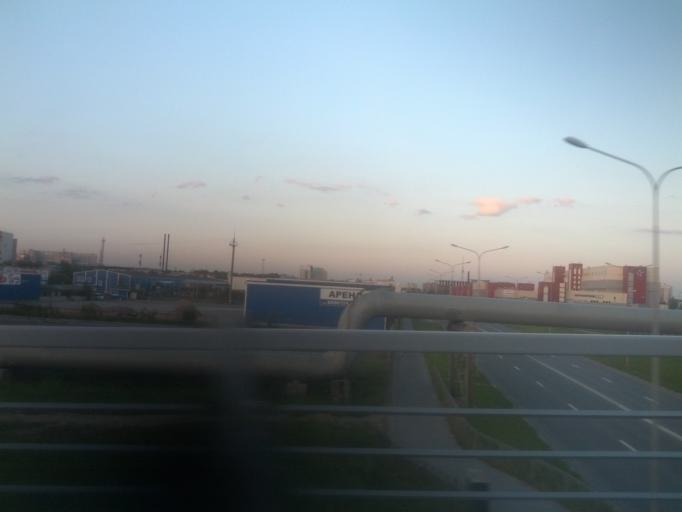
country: RU
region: St.-Petersburg
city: Staraya Derevnya
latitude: 59.9921
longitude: 30.2326
